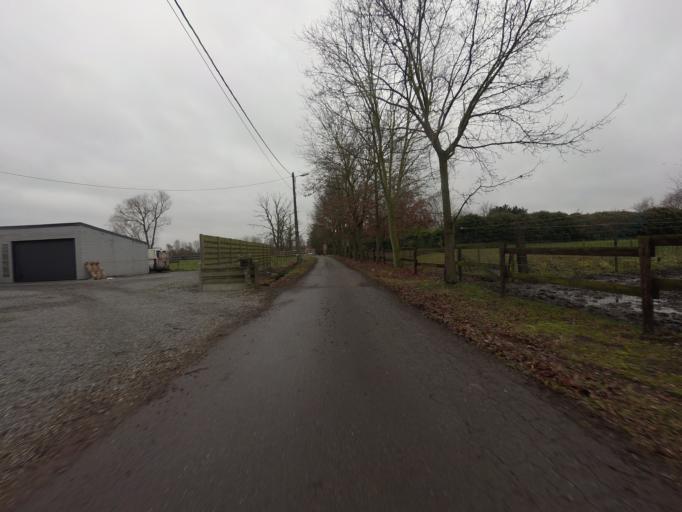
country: BE
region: Flanders
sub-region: Provincie Antwerpen
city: Sint-Katelijne-Waver
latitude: 51.0500
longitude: 4.5544
